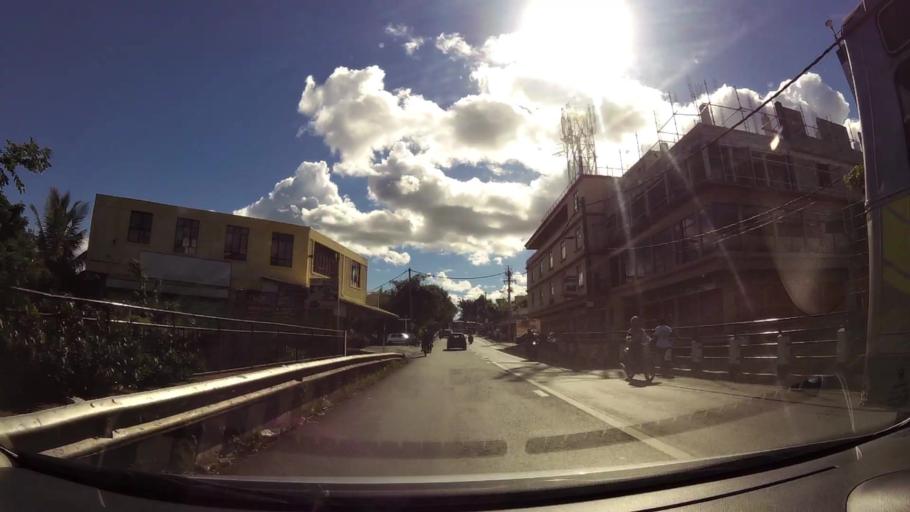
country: MU
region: Pamplemousses
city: Le Hochet
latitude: -20.1439
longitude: 57.5241
